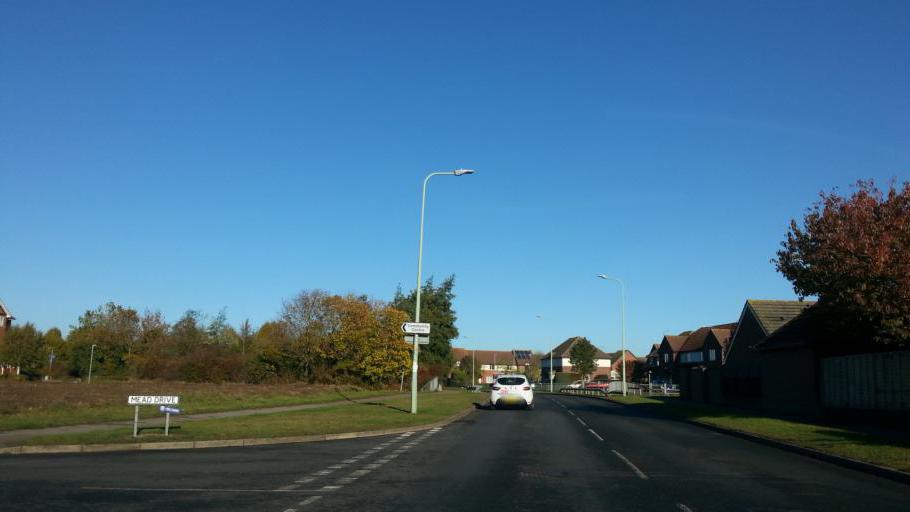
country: GB
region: England
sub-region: Suffolk
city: Kesgrave
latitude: 52.0607
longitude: 1.2388
